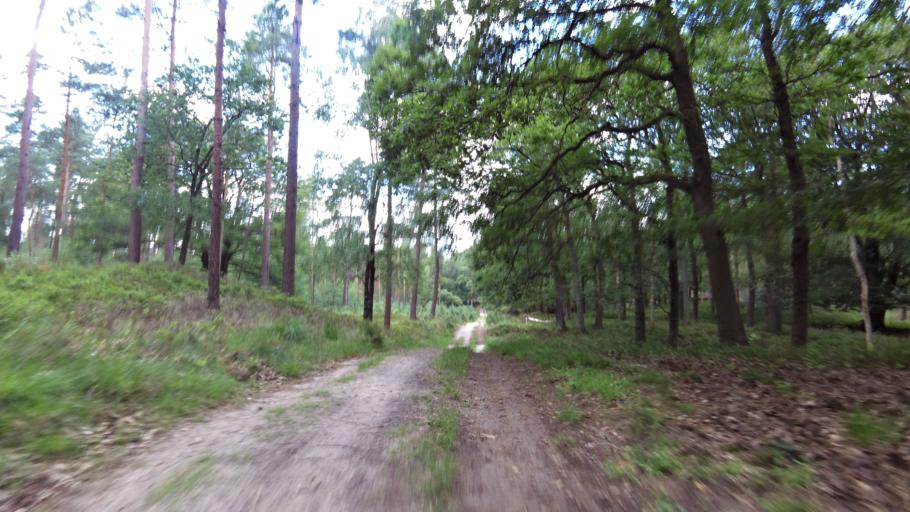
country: NL
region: Gelderland
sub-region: Gemeente Apeldoorn
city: Uddel
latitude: 52.2423
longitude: 5.8119
